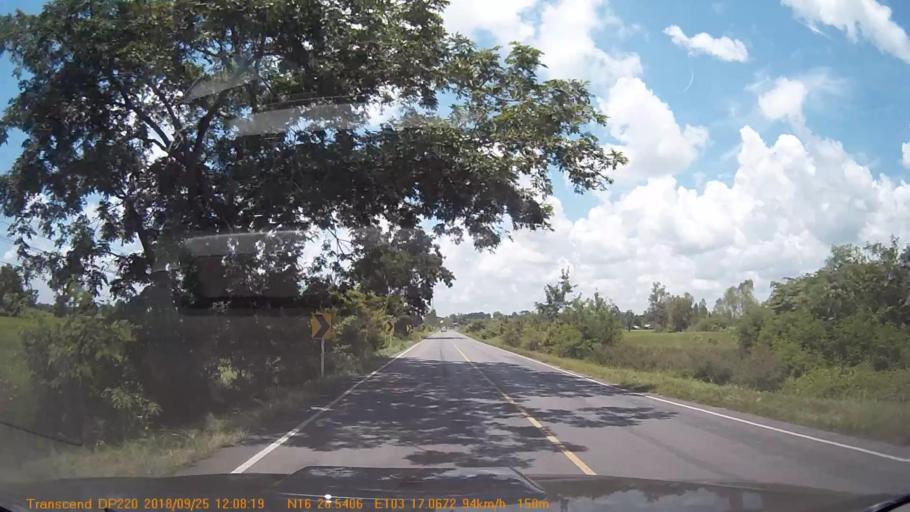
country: TH
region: Kalasin
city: Yang Talat
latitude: 16.4423
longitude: 103.2846
